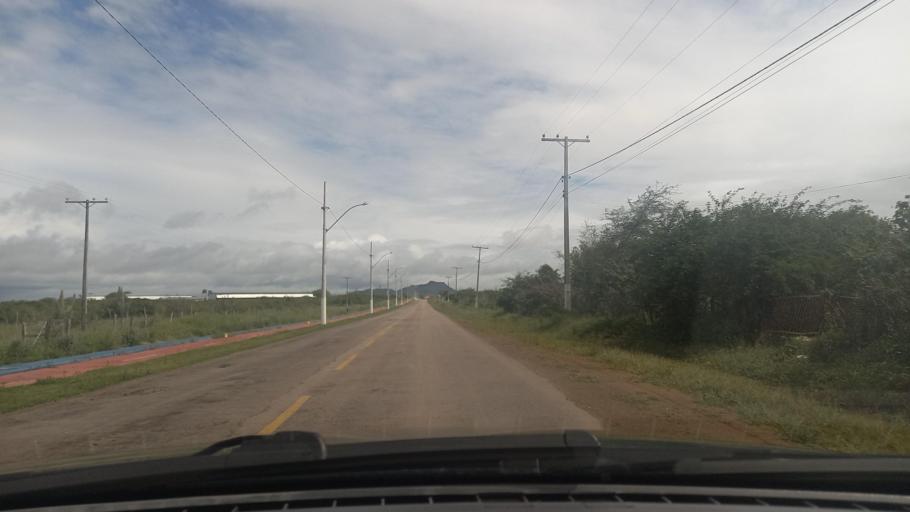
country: BR
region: Bahia
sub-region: Paulo Afonso
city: Paulo Afonso
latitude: -9.3538
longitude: -38.2662
